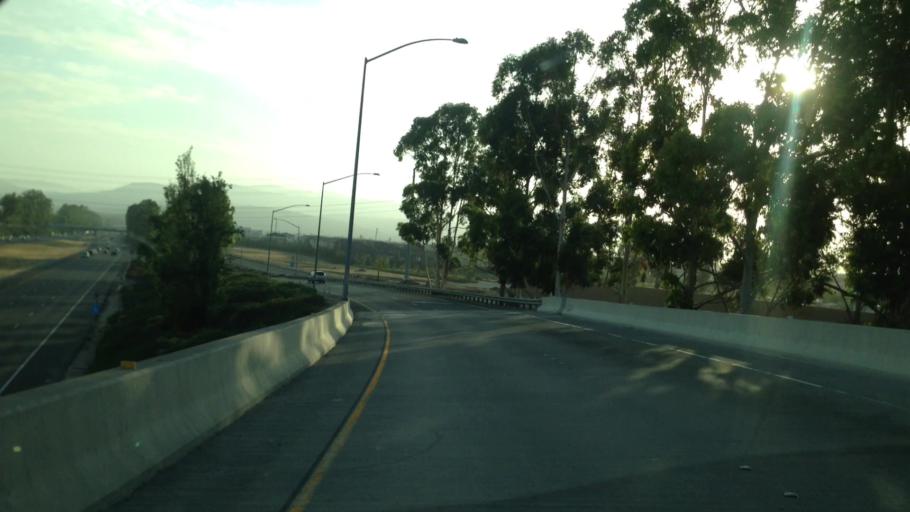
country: US
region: California
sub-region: Orange County
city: Lake Forest
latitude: 33.6771
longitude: -117.7518
